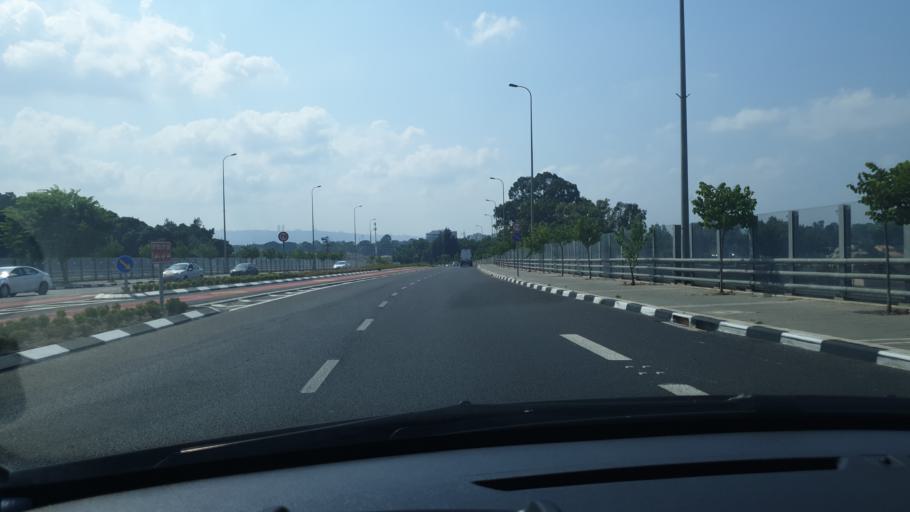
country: IL
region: Haifa
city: Qiryat Bialik
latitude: 32.8151
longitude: 35.0896
